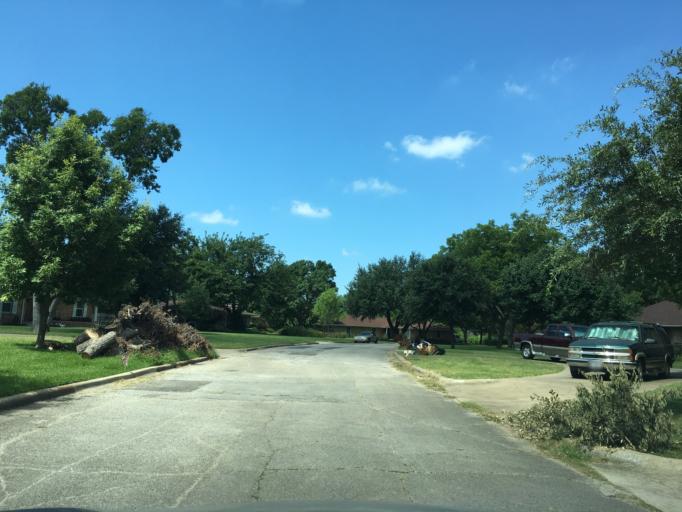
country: US
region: Texas
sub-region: Dallas County
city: Garland
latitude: 32.8402
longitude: -96.6538
